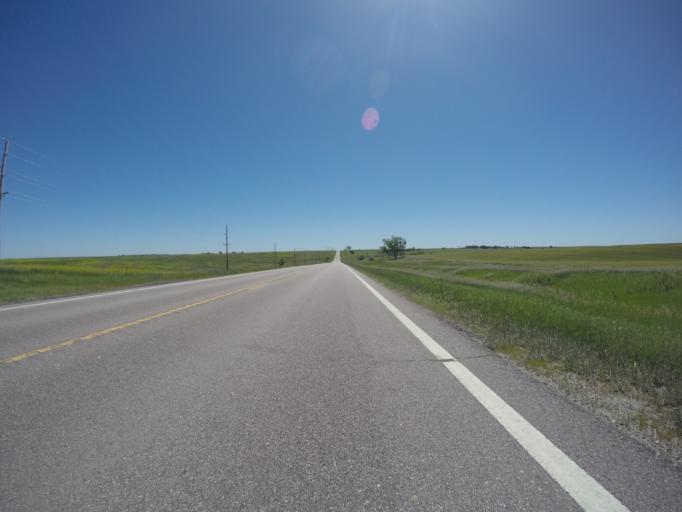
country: US
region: Kansas
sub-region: Norton County
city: Norton
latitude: 39.8284
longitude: -99.6708
